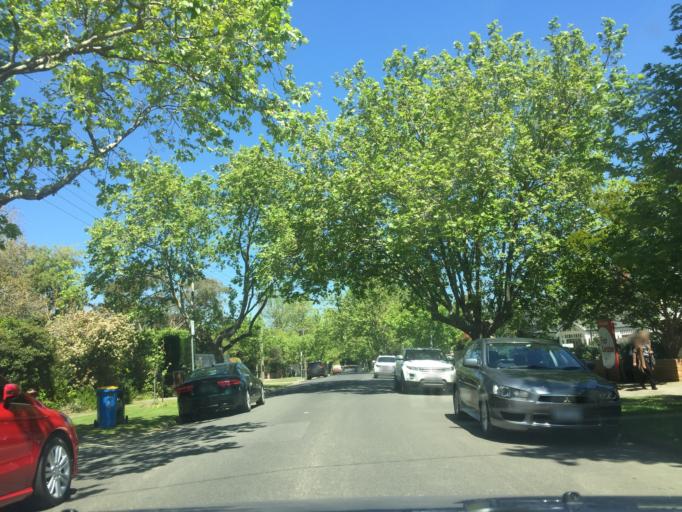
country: AU
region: Victoria
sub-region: Boroondara
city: Canterbury
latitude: -37.8206
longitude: 145.0847
